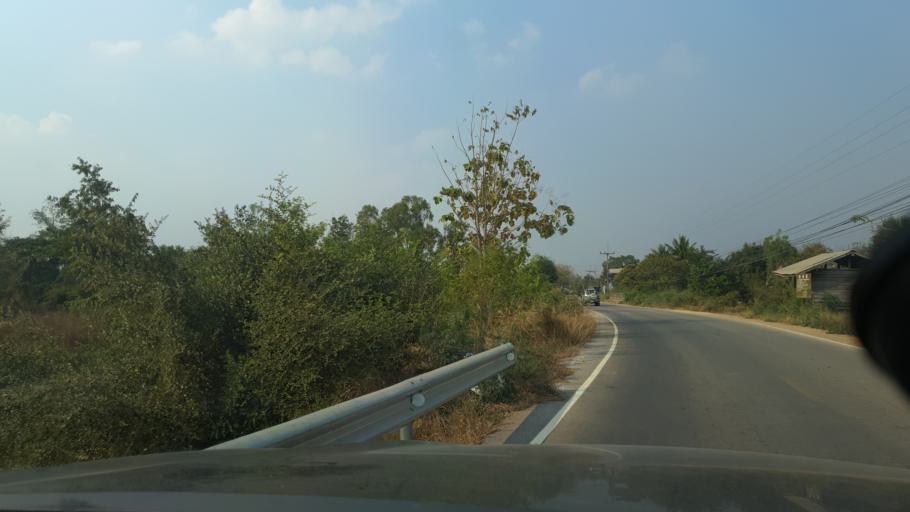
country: TH
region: Sukhothai
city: Ban Dan Lan Hoi
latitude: 17.1094
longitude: 99.5507
